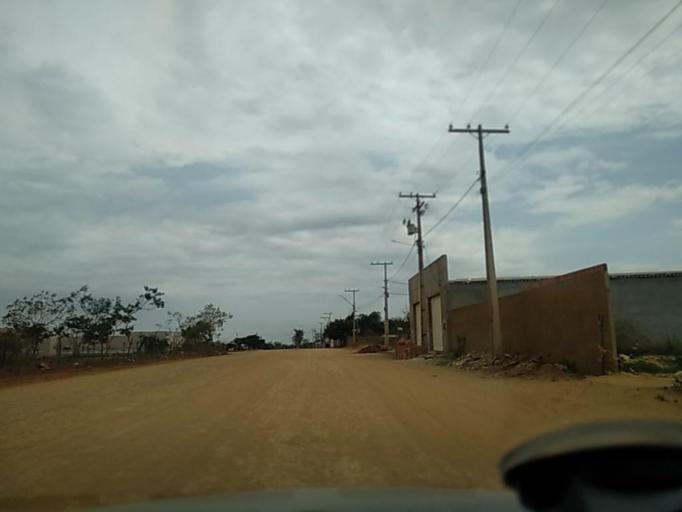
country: BR
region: Bahia
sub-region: Caetite
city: Caetite
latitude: -14.0526
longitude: -42.4728
